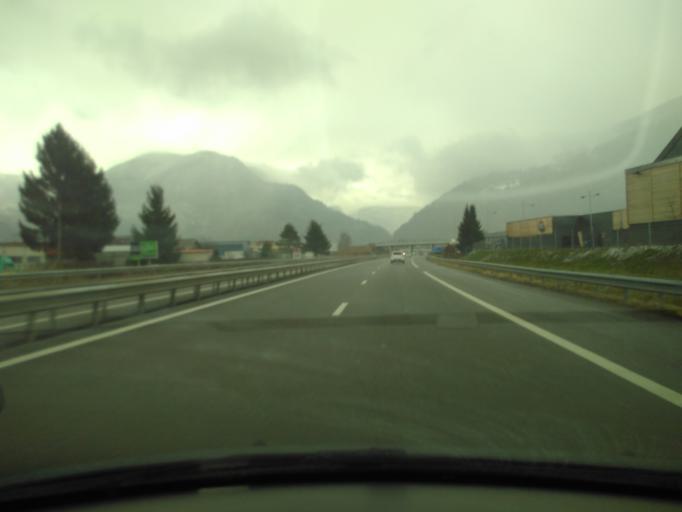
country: FR
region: Rhone-Alpes
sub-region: Departement de la Haute-Savoie
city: Scionzier
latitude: 46.0681
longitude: 6.5500
